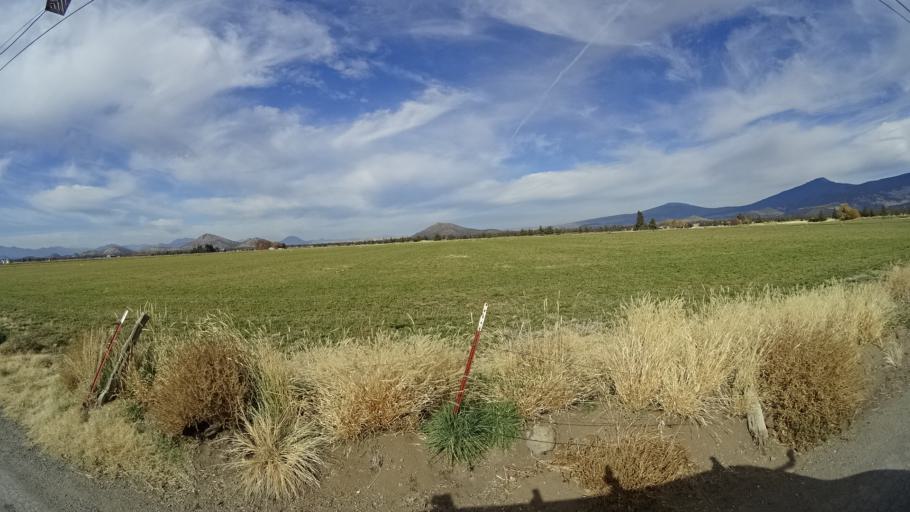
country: US
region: California
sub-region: Siskiyou County
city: Montague
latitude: 41.6166
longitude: -122.3848
